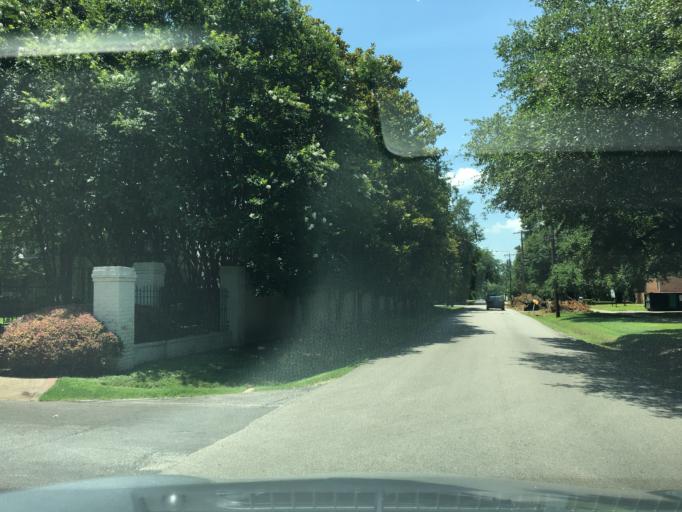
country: US
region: Texas
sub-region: Dallas County
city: University Park
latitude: 32.8782
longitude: -96.8085
